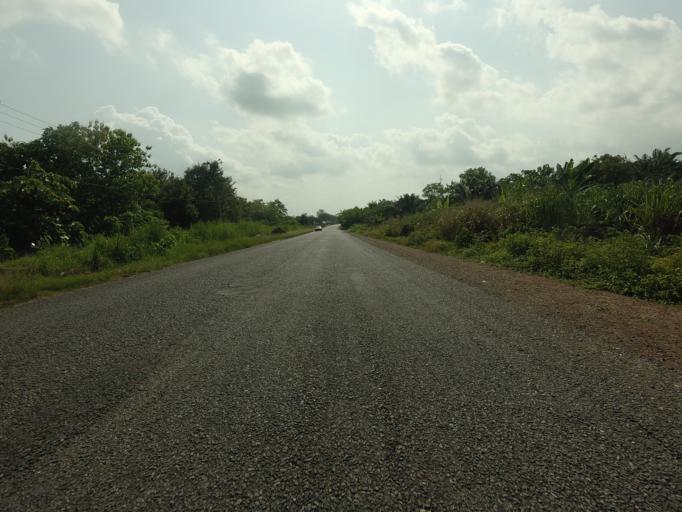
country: GH
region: Volta
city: Ho
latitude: 6.5753
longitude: 0.5900
